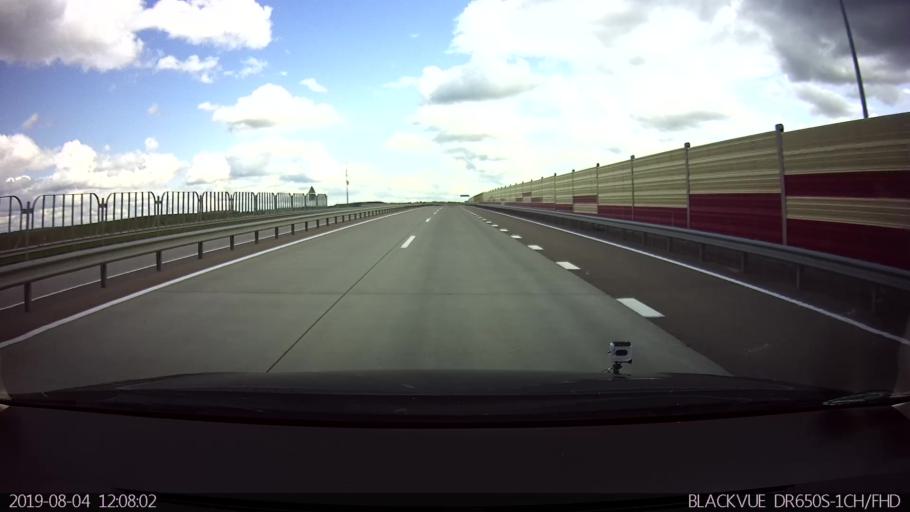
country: BY
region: Minsk
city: Syomkava
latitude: 54.0675
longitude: 27.4513
